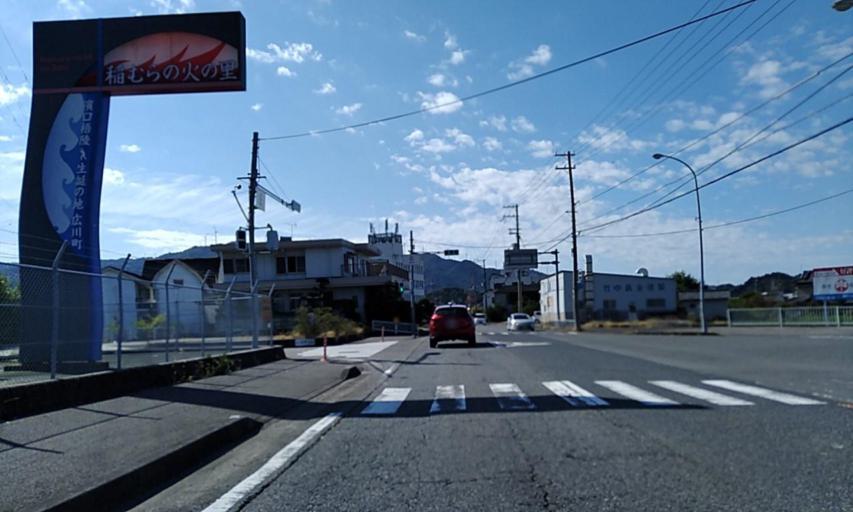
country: JP
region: Wakayama
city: Kainan
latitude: 34.0253
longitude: 135.1812
